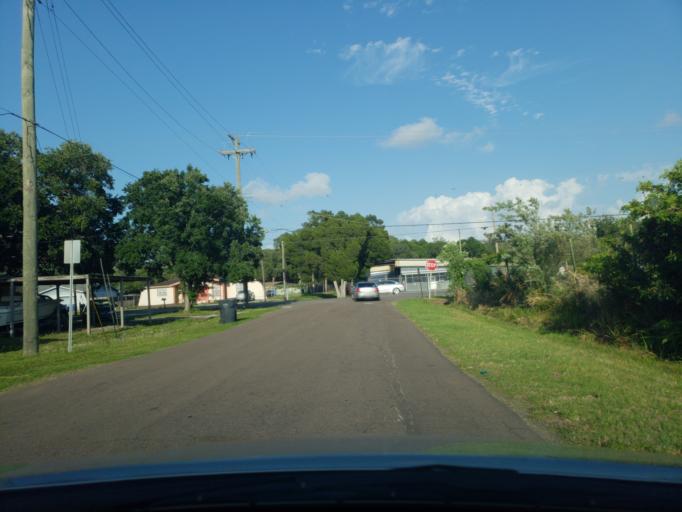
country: US
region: Florida
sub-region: Hillsborough County
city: Palm River-Clair Mel
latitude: 27.9155
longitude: -82.3692
